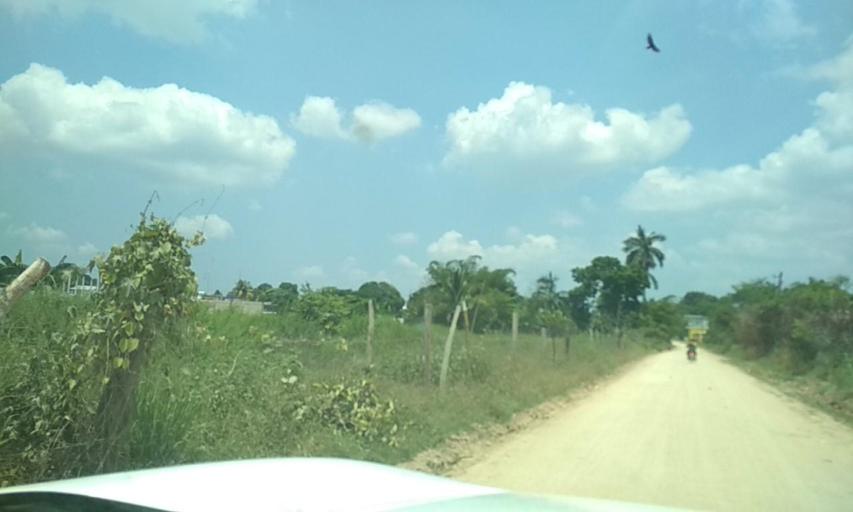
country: MX
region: Veracruz
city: Las Choapas
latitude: 17.9158
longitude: -94.0882
